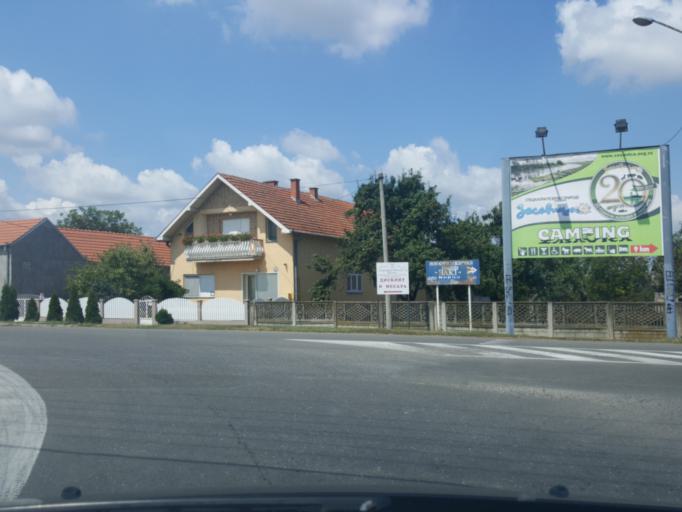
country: RS
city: Macvanska Mitrovica
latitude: 44.9565
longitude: 19.6004
